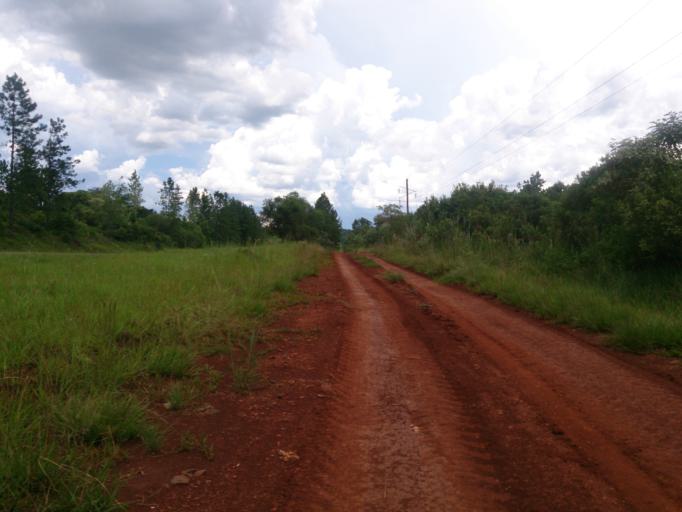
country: AR
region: Misiones
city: Campo Viera
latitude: -27.3609
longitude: -55.0503
